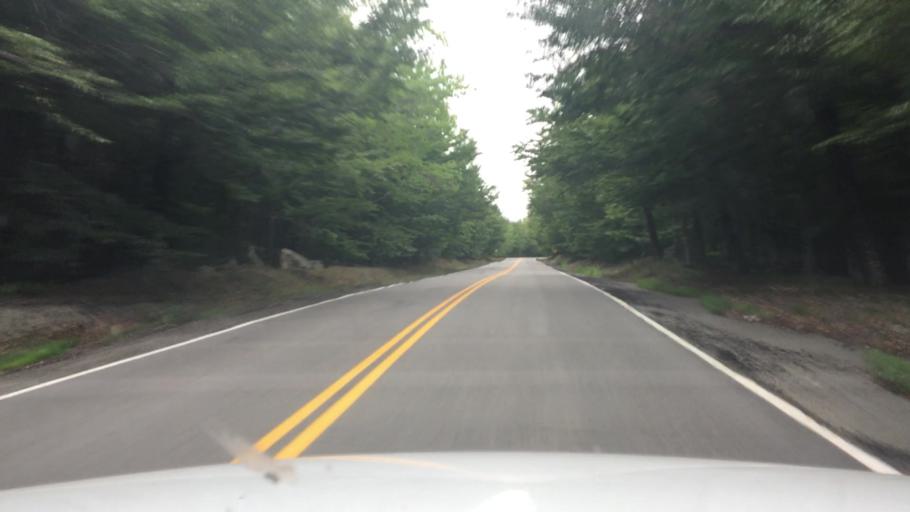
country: US
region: Maine
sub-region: Hancock County
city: Gouldsboro
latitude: 44.6121
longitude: -68.0659
